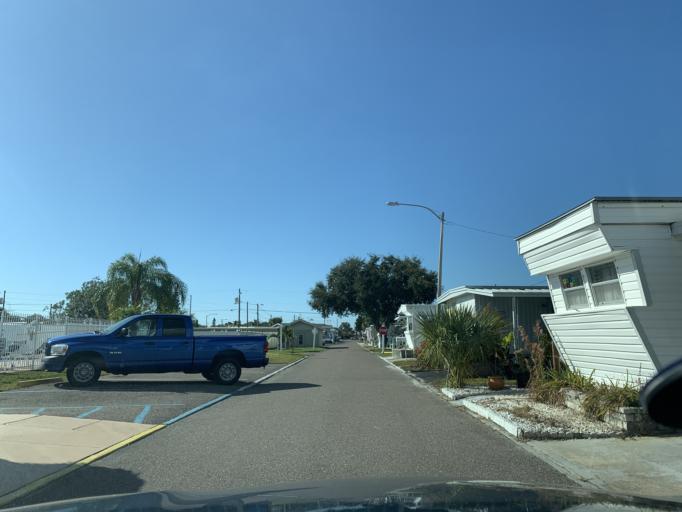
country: US
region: Florida
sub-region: Pinellas County
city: Bay Pines
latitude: 27.8114
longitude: -82.7510
